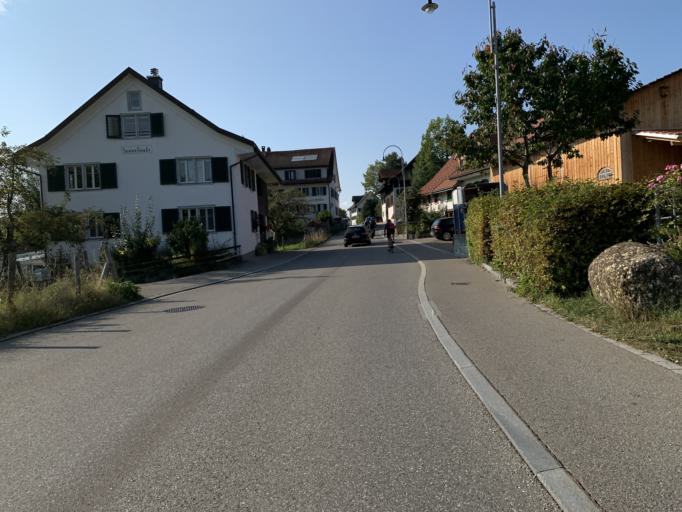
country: CH
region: Zurich
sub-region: Bezirk Hinwil
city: Baretswil
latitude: 47.3155
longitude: 8.8546
